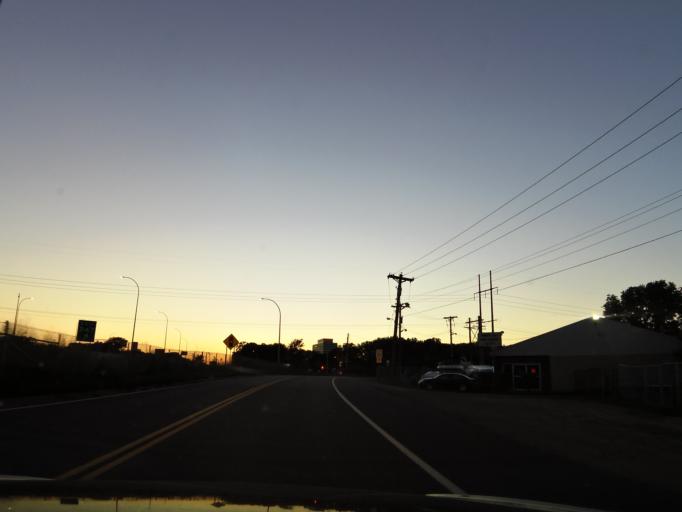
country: US
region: Minnesota
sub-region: Ramsey County
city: Maplewood
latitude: 44.9487
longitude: -92.9834
